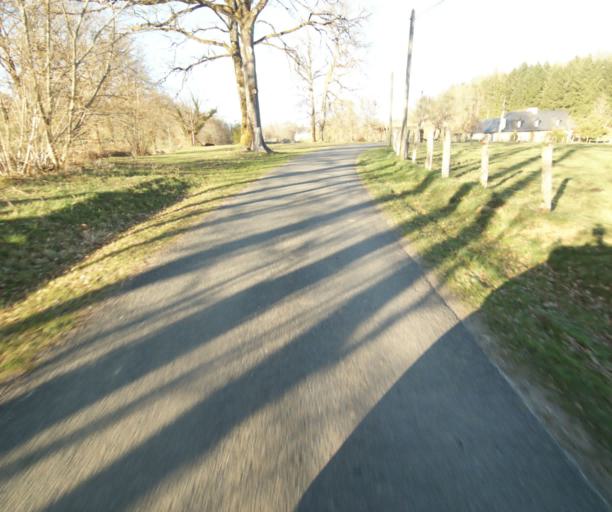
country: FR
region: Limousin
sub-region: Departement de la Correze
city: Saint-Clement
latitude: 45.3636
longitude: 1.6860
